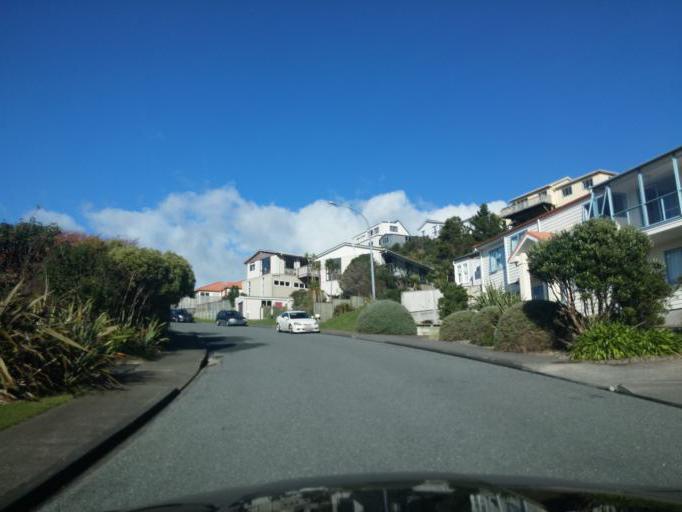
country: NZ
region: Wellington
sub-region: Wellington City
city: Wellington
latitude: -41.2346
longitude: 174.7925
